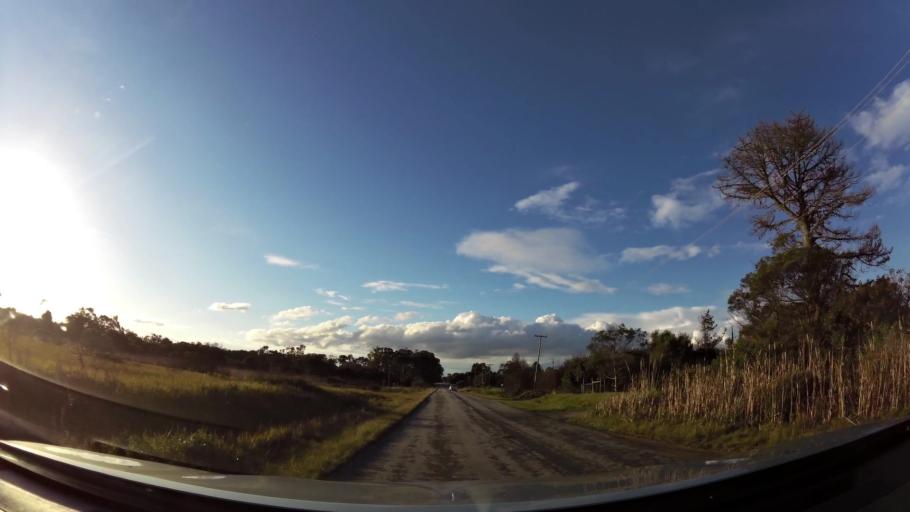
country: ZA
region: Eastern Cape
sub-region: Nelson Mandela Bay Metropolitan Municipality
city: Port Elizabeth
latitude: -33.9836
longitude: 25.4840
